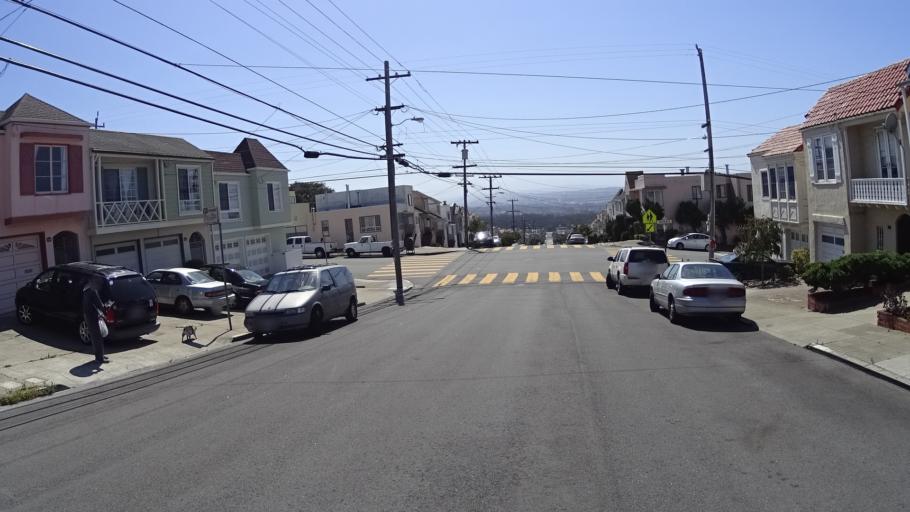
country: US
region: California
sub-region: San Mateo County
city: Daly City
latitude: 37.7469
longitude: -122.4824
